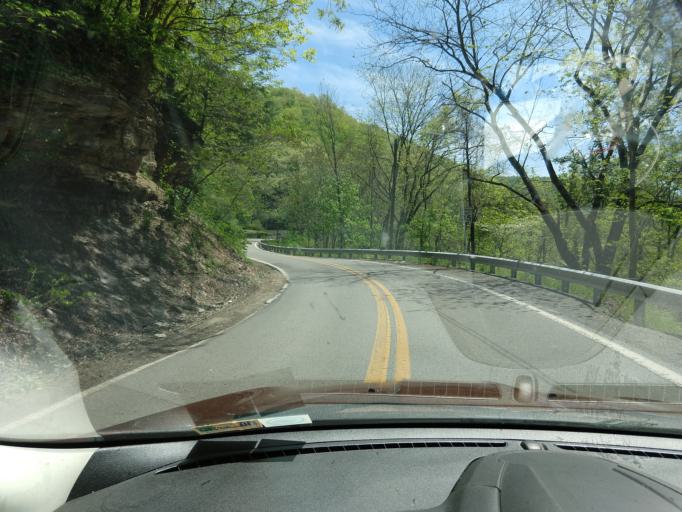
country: US
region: West Virginia
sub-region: McDowell County
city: Welch
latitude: 37.3131
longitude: -81.6949
